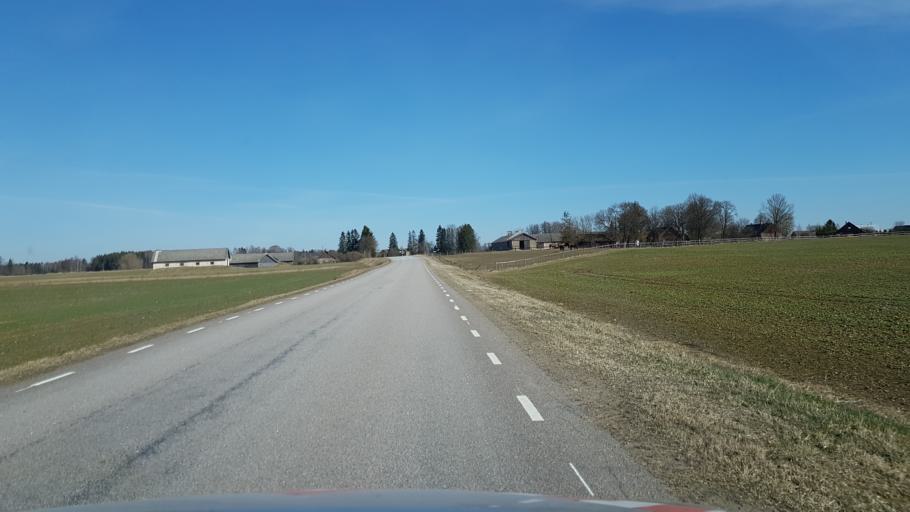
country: EE
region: Laeaene-Virumaa
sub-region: Vinni vald
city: Vinni
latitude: 59.2486
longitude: 26.3554
